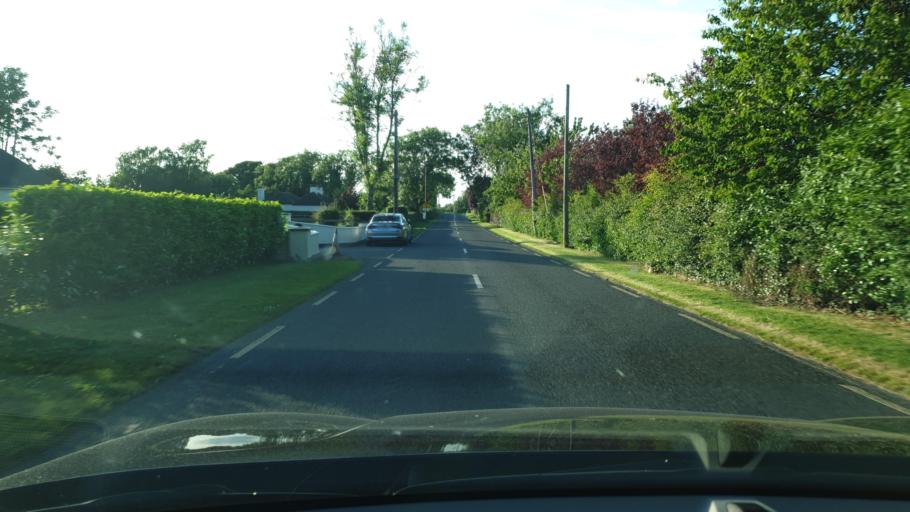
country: IE
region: Leinster
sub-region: An Mhi
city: Ratoath
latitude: 53.4951
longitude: -6.4389
